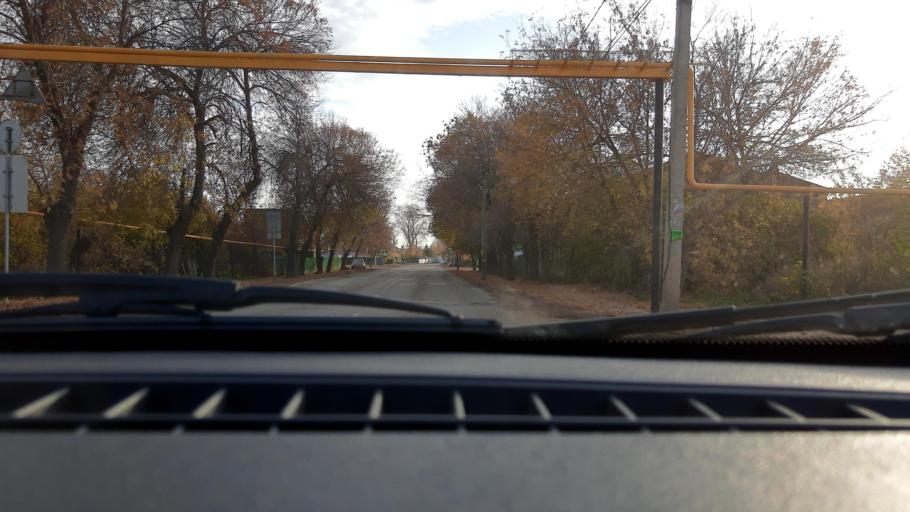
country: RU
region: Bashkortostan
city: Mikhaylovka
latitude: 54.7433
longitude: 55.8989
